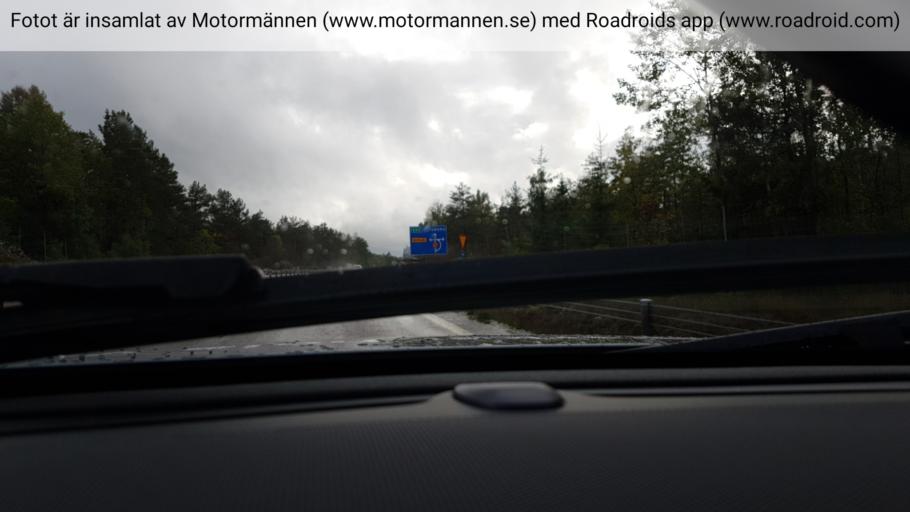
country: SE
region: Vaestra Goetaland
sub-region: Melleruds Kommun
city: Mellerud
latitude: 58.7568
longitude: 12.4898
